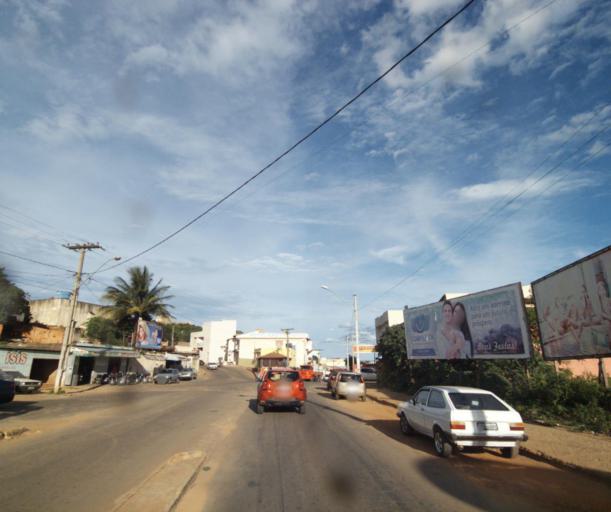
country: BR
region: Bahia
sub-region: Caetite
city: Caetite
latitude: -14.0649
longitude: -42.4863
